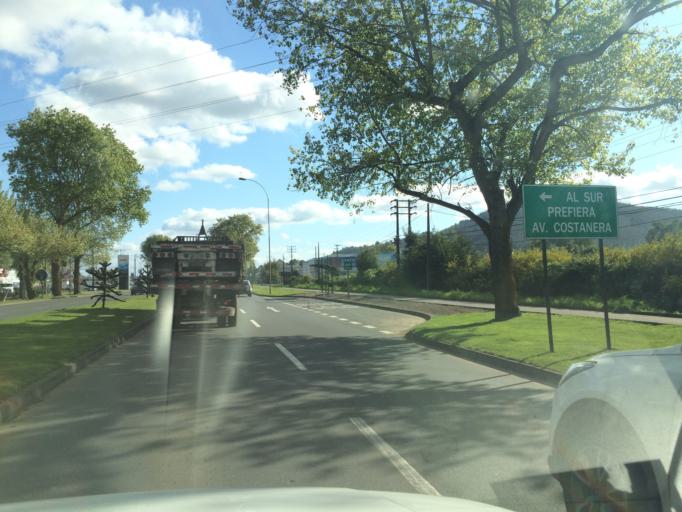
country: CL
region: Araucania
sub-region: Provincia de Cautin
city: Temuco
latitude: -38.7095
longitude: -72.5571
